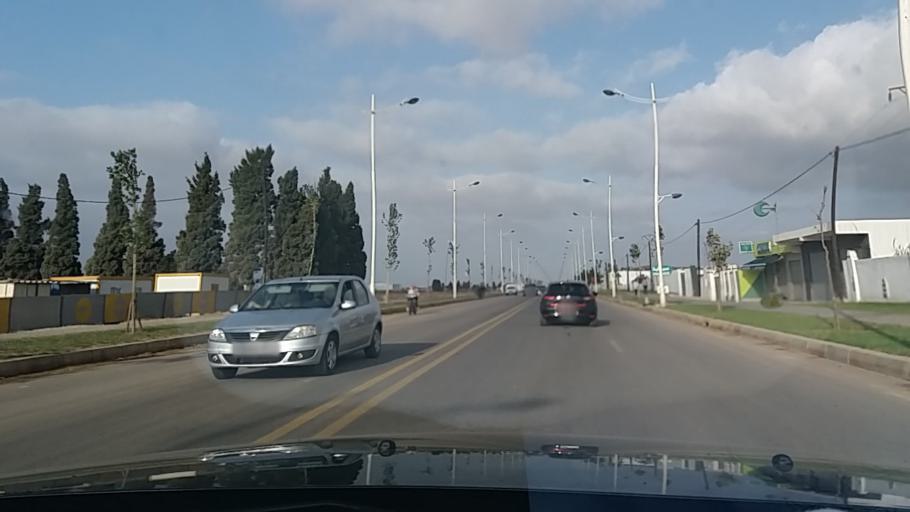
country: MA
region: Tanger-Tetouan
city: Tetouan
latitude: 35.5680
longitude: -5.3359
